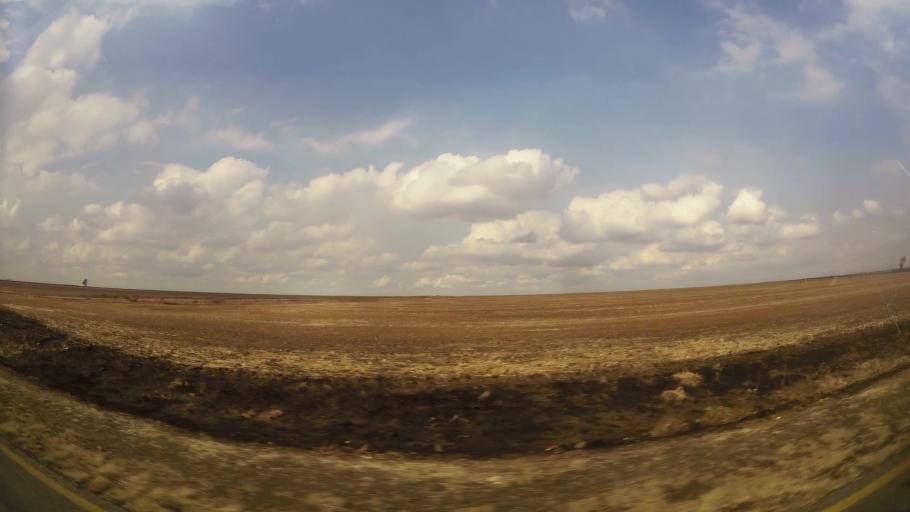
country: ZA
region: Orange Free State
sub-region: Fezile Dabi District Municipality
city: Sasolburg
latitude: -26.8389
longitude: 27.8941
